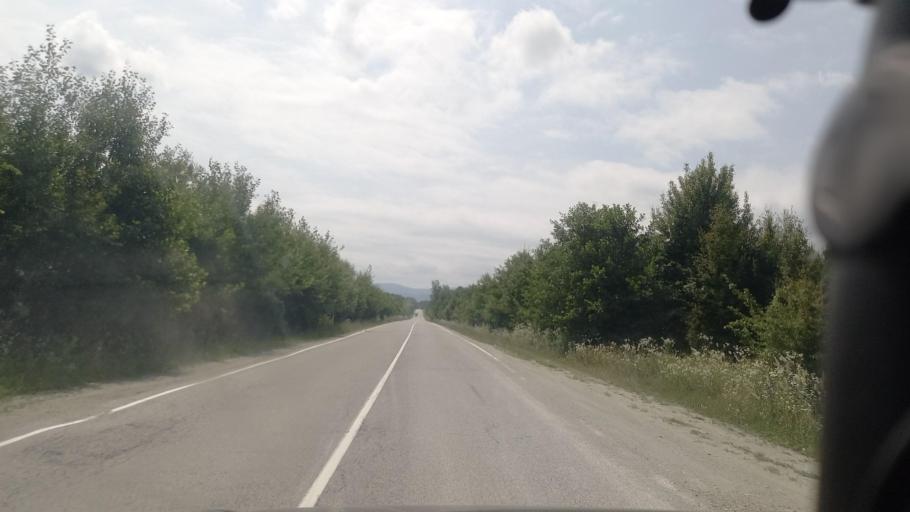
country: RU
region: Karachayevo-Cherkesiya
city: Kurdzhinovo
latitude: 44.0258
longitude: 40.9276
